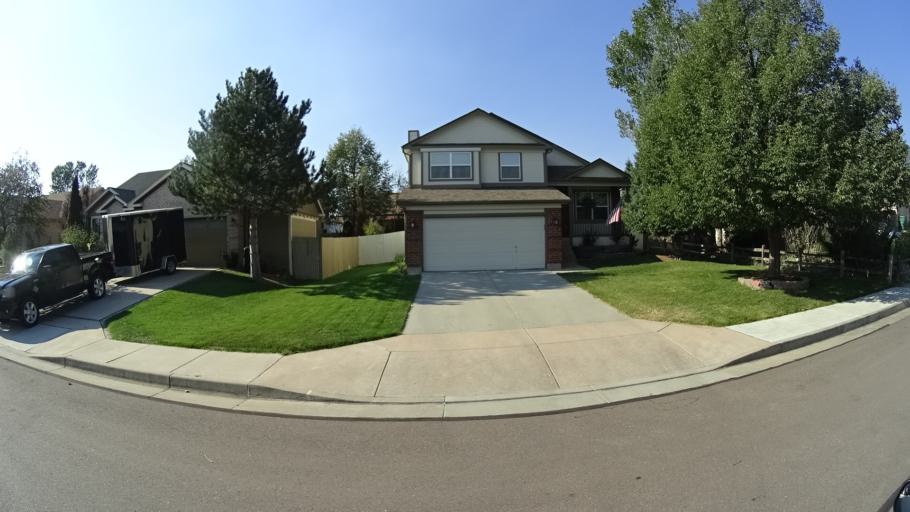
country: US
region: Colorado
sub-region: El Paso County
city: Stratmoor
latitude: 38.7709
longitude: -104.8043
